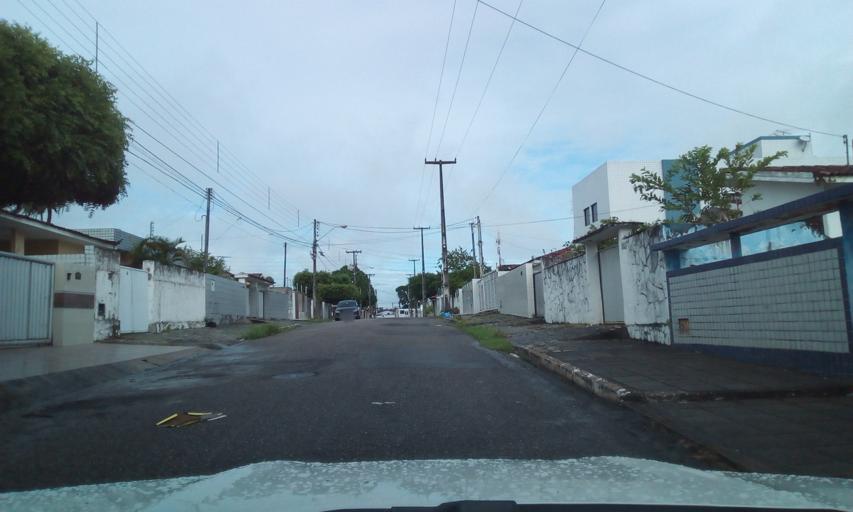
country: BR
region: Paraiba
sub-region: Joao Pessoa
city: Joao Pessoa
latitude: -7.1510
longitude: -34.8770
